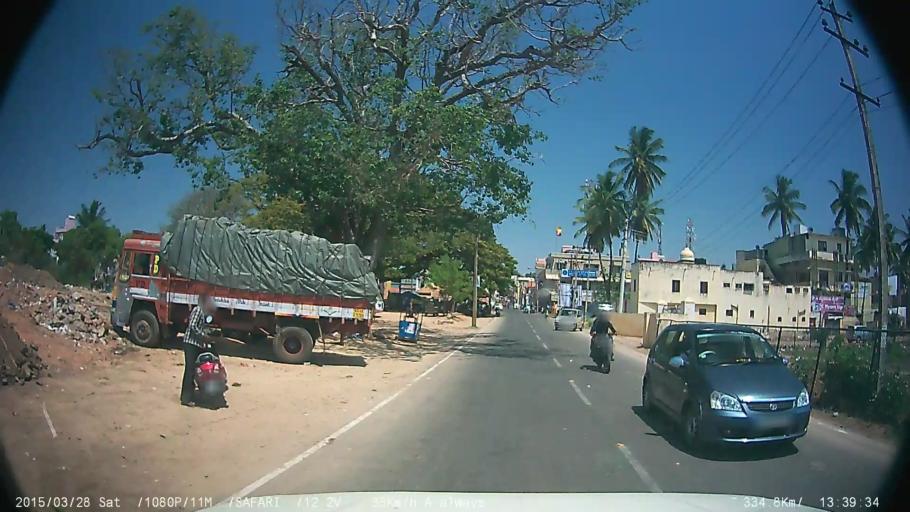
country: IN
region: Karnataka
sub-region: Mysore
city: Mysore
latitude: 12.3039
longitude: 76.6607
